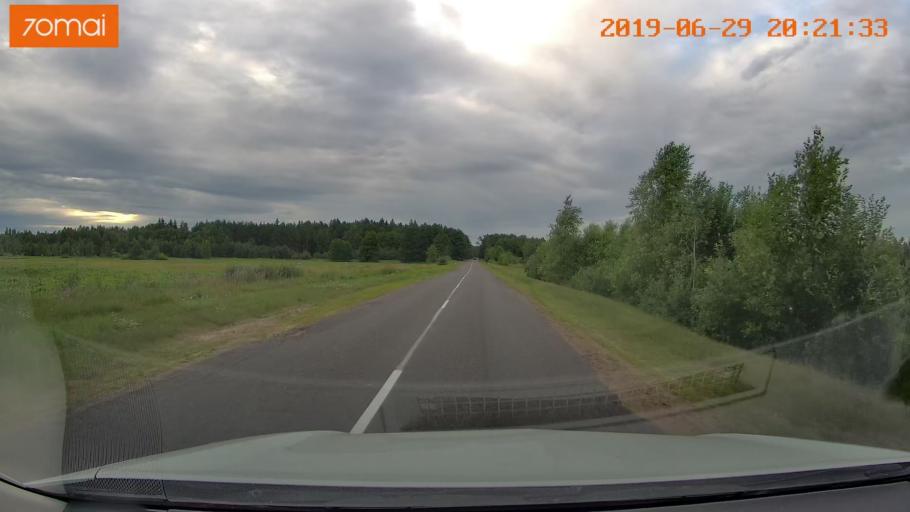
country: BY
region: Brest
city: Asnyezhytsy
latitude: 52.4211
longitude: 26.2531
